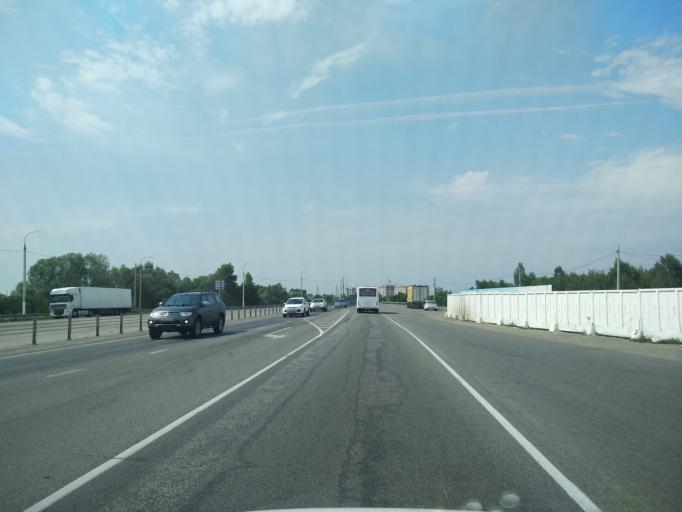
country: RU
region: Voronezj
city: Somovo
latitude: 51.6811
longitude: 39.3435
